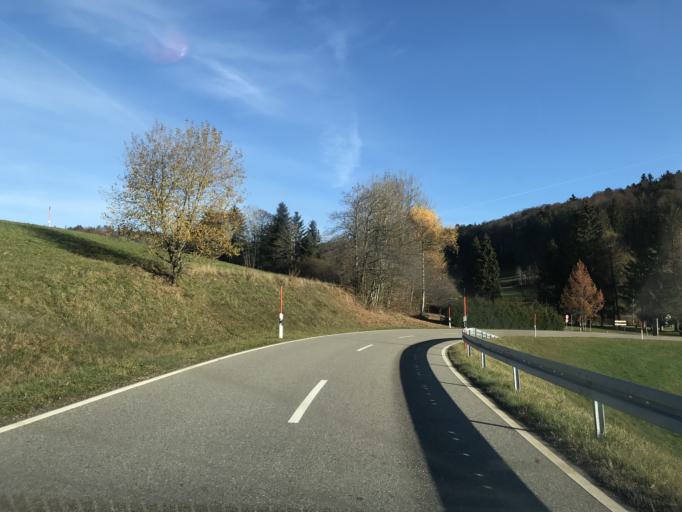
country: DE
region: Baden-Wuerttemberg
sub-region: Freiburg Region
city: Rickenbach
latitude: 47.6415
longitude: 7.9568
